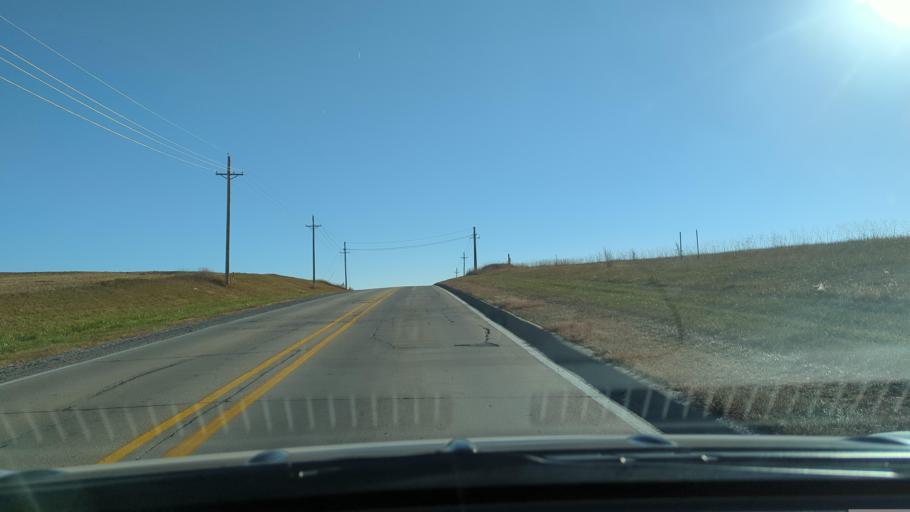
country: US
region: Nebraska
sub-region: Sarpy County
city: Papillion
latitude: 41.0928
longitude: -96.0059
